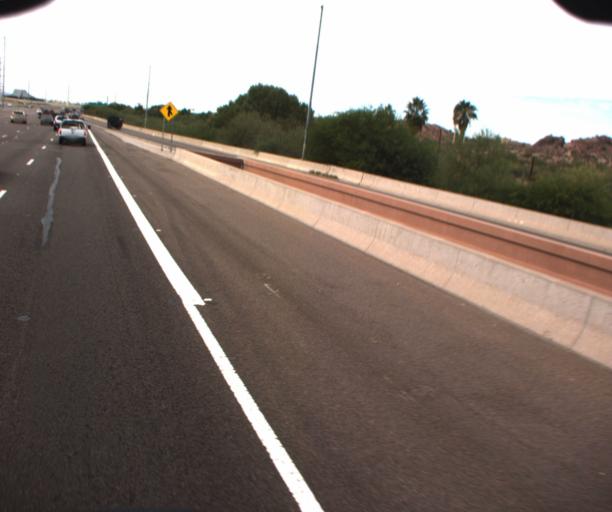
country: US
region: Arizona
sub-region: Maricopa County
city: Tempe Junction
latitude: 33.4360
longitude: -111.9304
